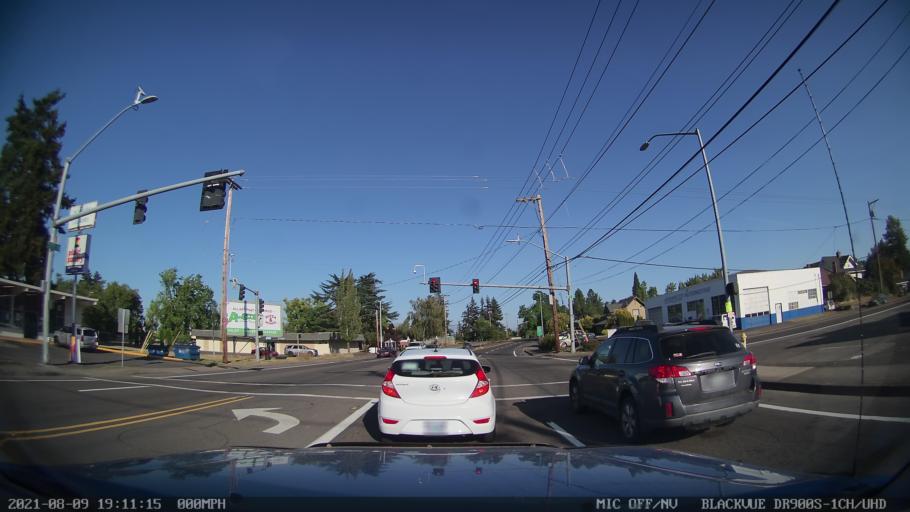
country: US
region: Oregon
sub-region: Marion County
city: Four Corners
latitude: 44.9325
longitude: -123.0101
